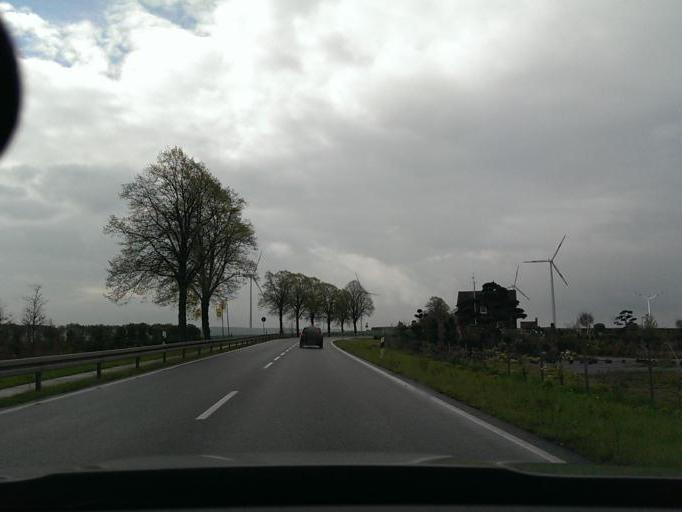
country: DE
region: Lower Saxony
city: Nordstemmen
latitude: 52.2036
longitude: 9.7477
